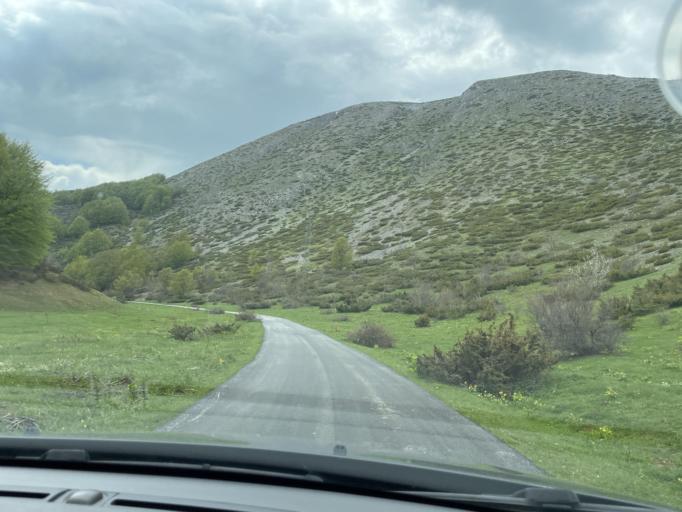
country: MK
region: Opstina Rostusa
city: Rostusha
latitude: 41.6013
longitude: 20.6805
